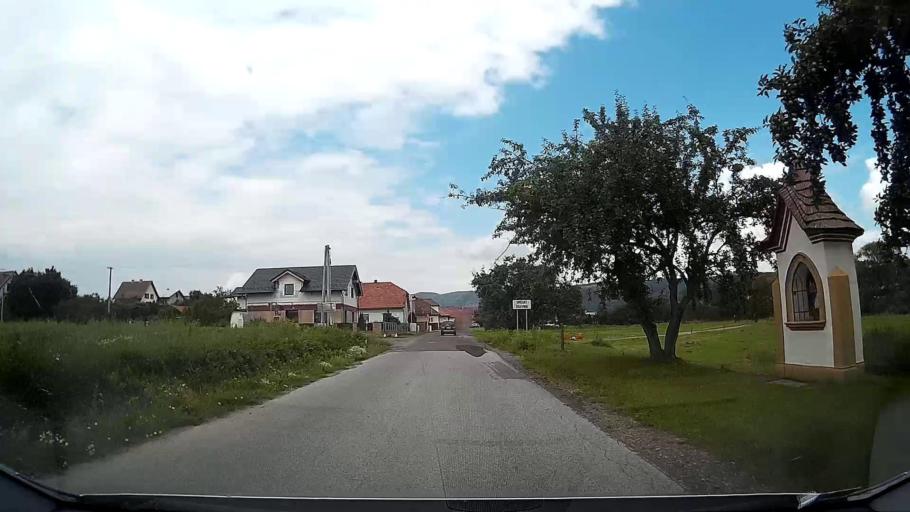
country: SK
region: Presovsky
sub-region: Okres Poprad
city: Poprad
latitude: 48.9885
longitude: 20.3673
